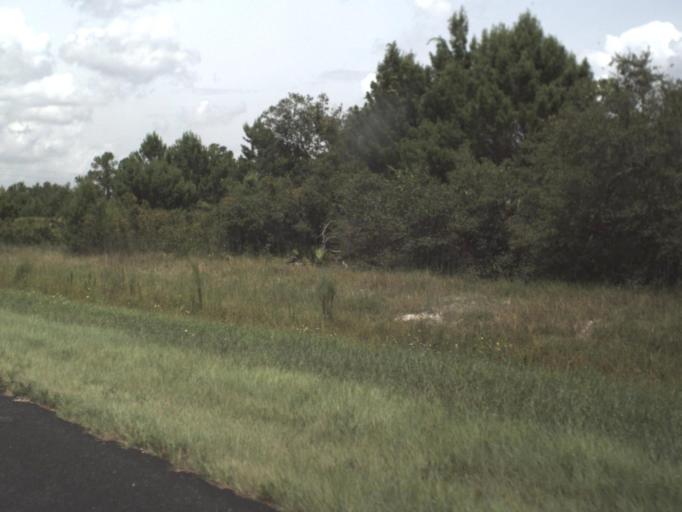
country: US
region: Florida
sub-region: Polk County
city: Frostproof
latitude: 27.7230
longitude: -81.5650
